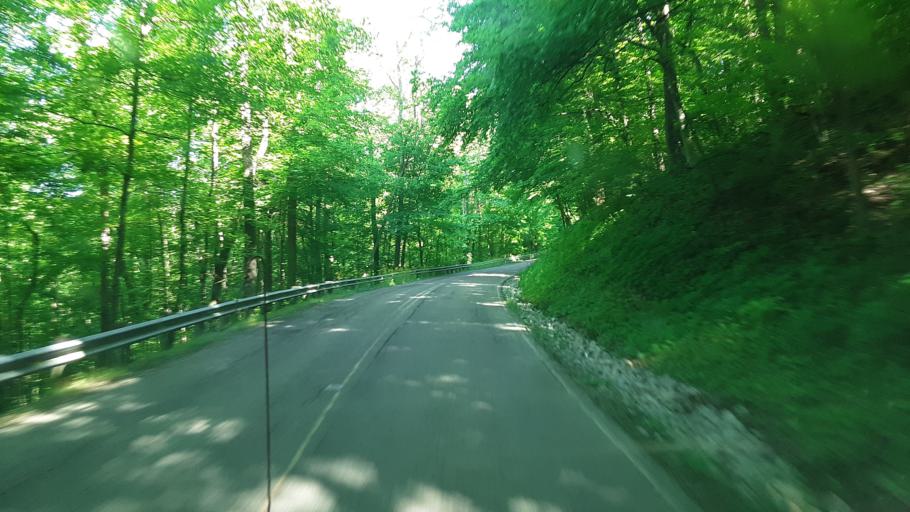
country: US
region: Ohio
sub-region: Tuscarawas County
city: Newcomerstown
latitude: 40.1797
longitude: -81.5513
